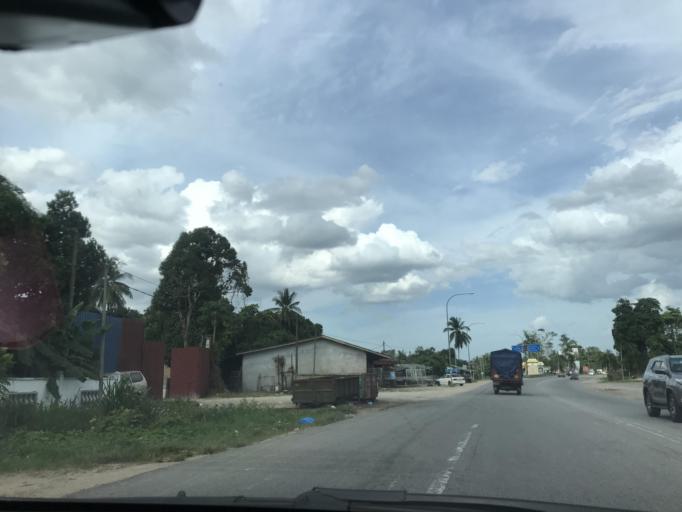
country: MY
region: Kelantan
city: Kampung Lemal
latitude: 6.0341
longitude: 102.1577
